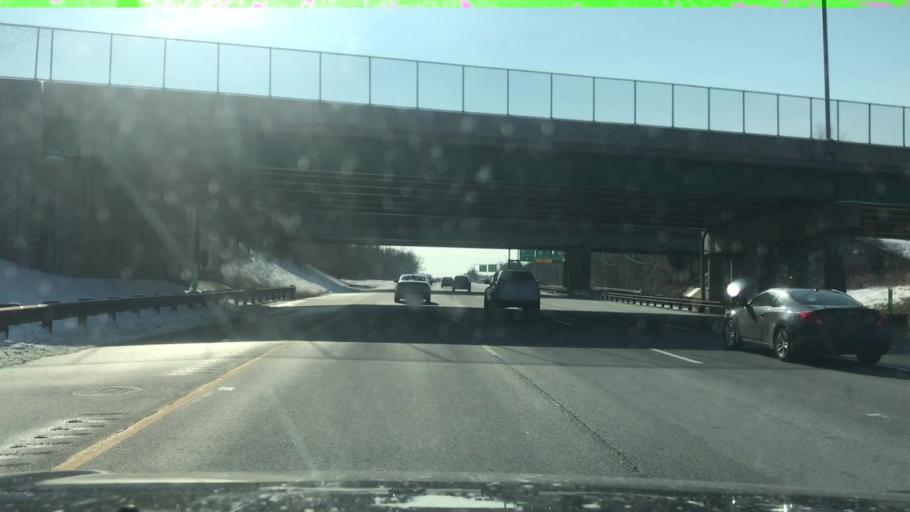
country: US
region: New Jersey
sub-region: Monmouth County
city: Shark River Hills
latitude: 40.1708
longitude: -74.1008
